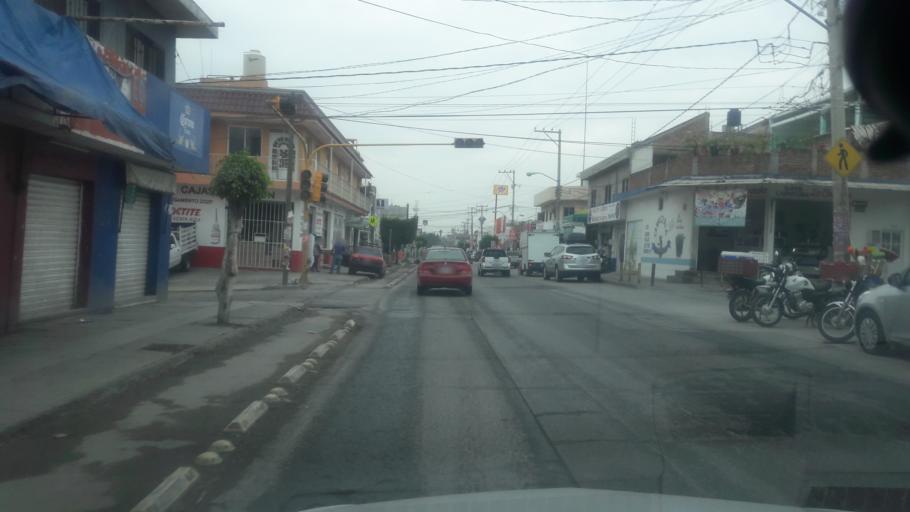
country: MX
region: Guanajuato
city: Leon
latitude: 21.1358
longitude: -101.7035
